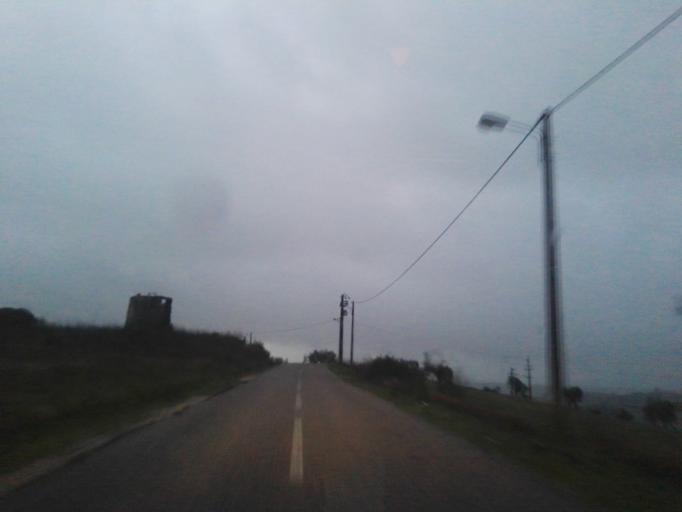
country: PT
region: Santarem
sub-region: Santarem
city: Santarem
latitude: 39.2978
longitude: -8.7779
